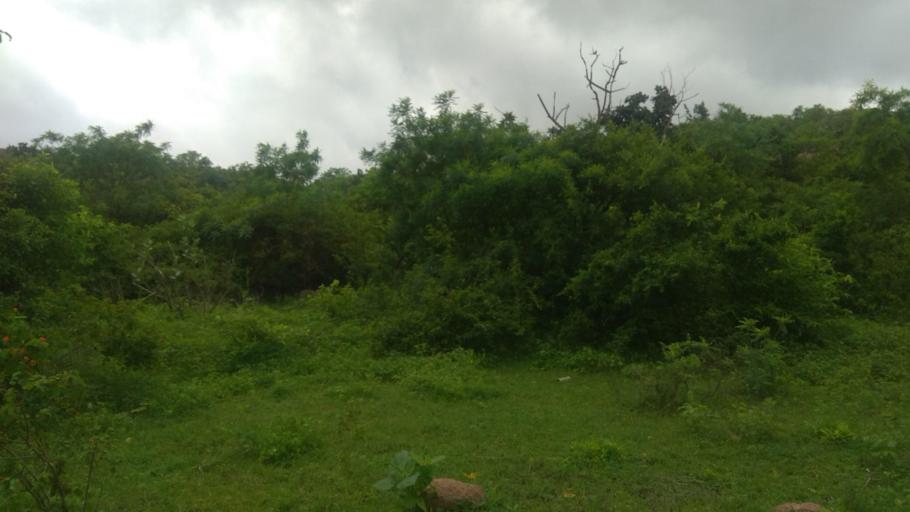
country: IN
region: Telangana
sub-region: Mahbubnagar
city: Farrukhnagar
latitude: 16.8971
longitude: 78.4978
